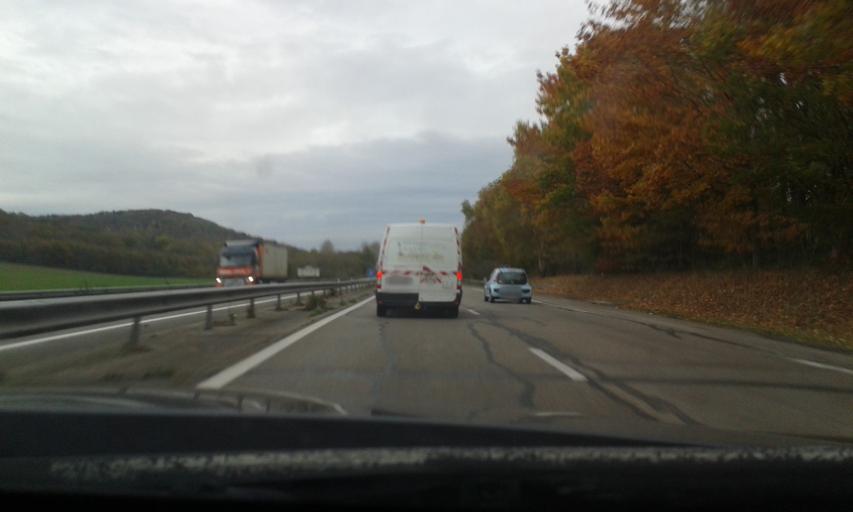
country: FR
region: Haute-Normandie
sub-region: Departement de l'Eure
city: Acquigny
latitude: 49.1752
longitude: 1.1701
